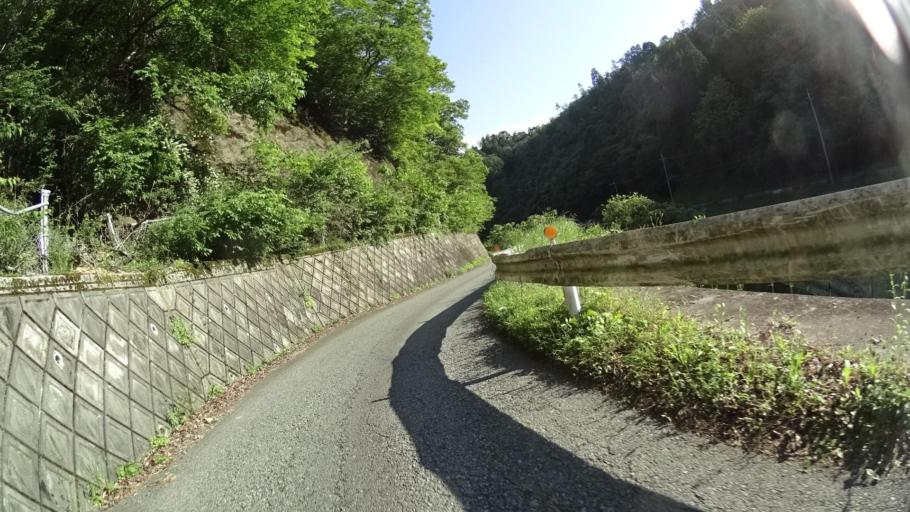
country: JP
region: Kyoto
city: Kameoka
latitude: 34.9713
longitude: 135.5621
